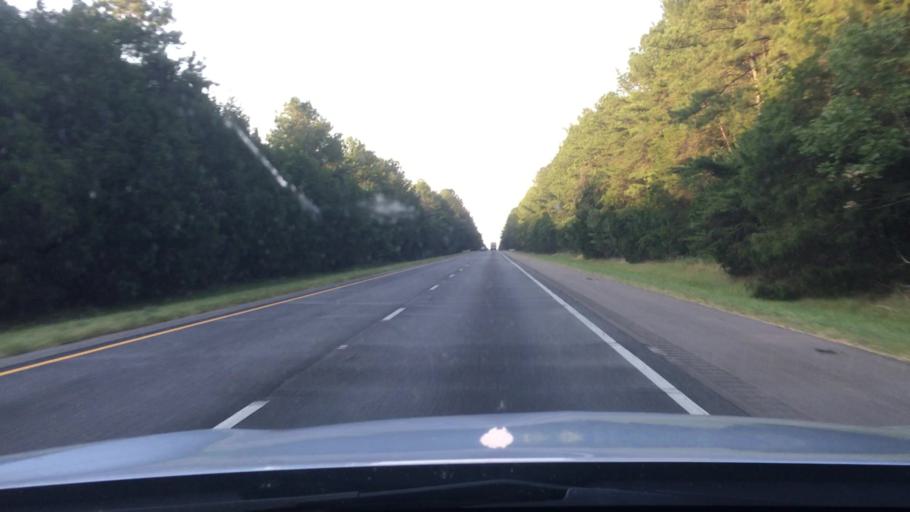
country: US
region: Alabama
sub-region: DeKalb County
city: Fort Payne
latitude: 34.3991
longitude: -85.7833
